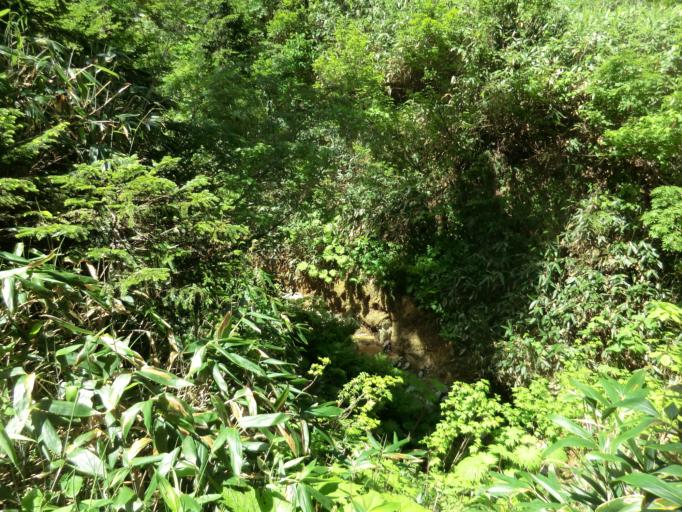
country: JP
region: Gunma
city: Numata
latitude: 36.8878
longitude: 139.1752
